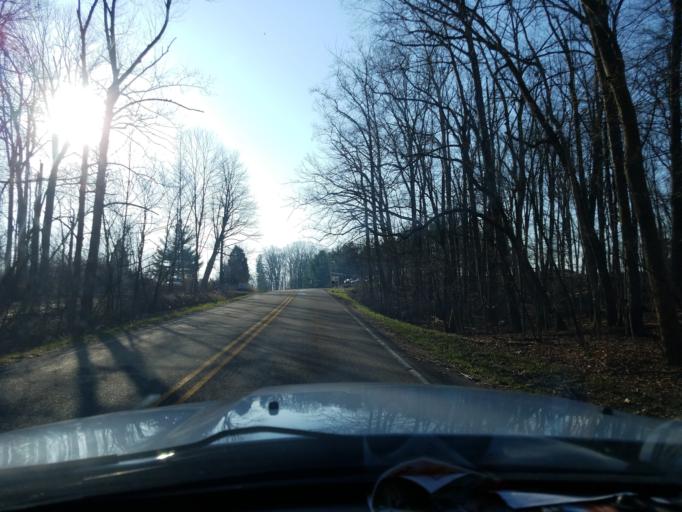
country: US
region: Indiana
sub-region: Owen County
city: Spencer
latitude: 39.3430
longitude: -86.9068
